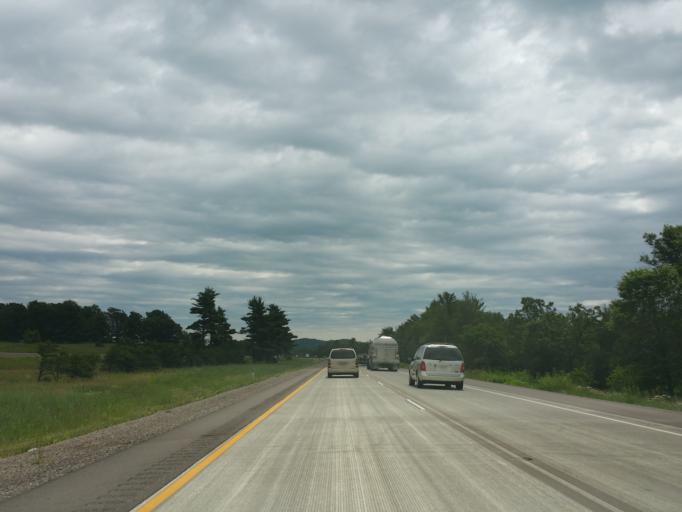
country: US
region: Wisconsin
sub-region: Jackson County
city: Black River Falls
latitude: 44.3686
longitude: -90.9746
